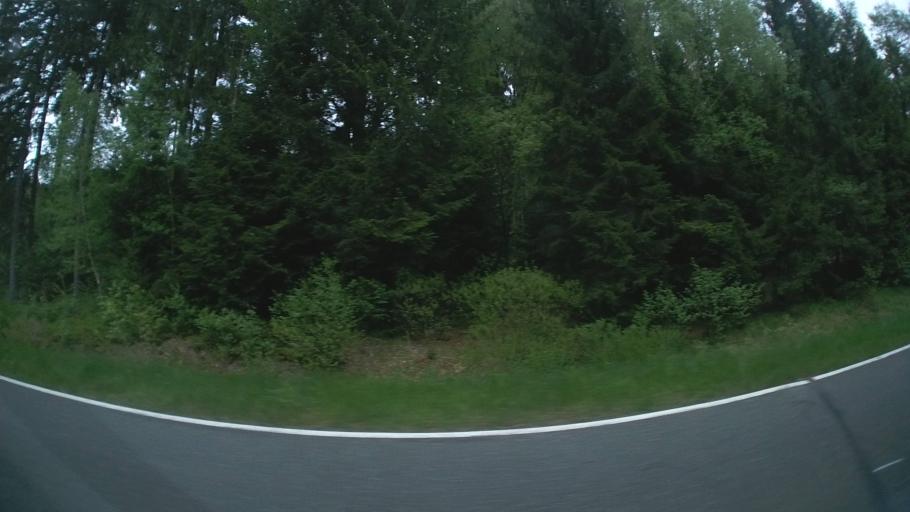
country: DE
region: Bavaria
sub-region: Upper Franconia
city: Zell im Fichtelgebirge
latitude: 50.1411
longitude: 11.8329
